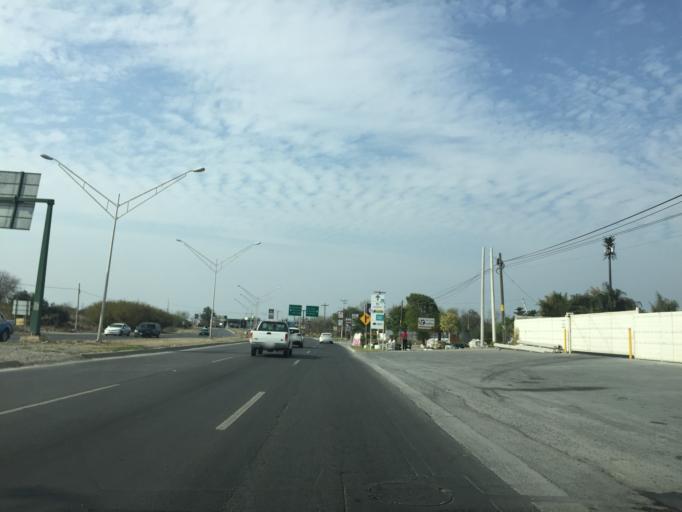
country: MX
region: Nuevo Leon
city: Apodaca
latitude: 25.7703
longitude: -100.1994
